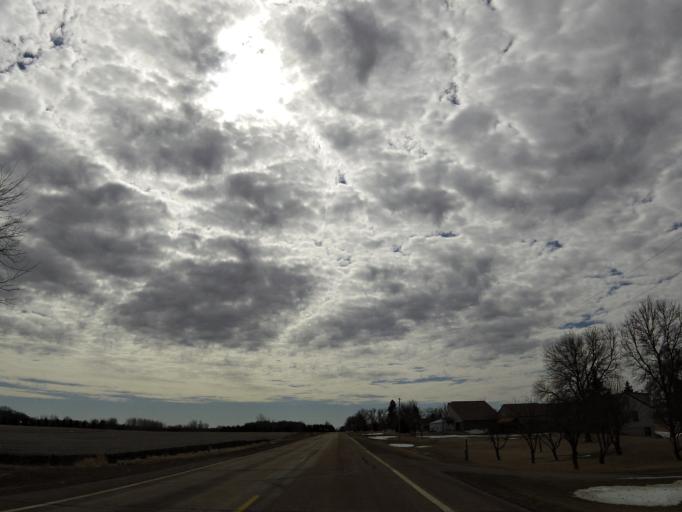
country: US
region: Minnesota
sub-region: Scott County
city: Prior Lake
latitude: 44.6562
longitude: -93.5165
